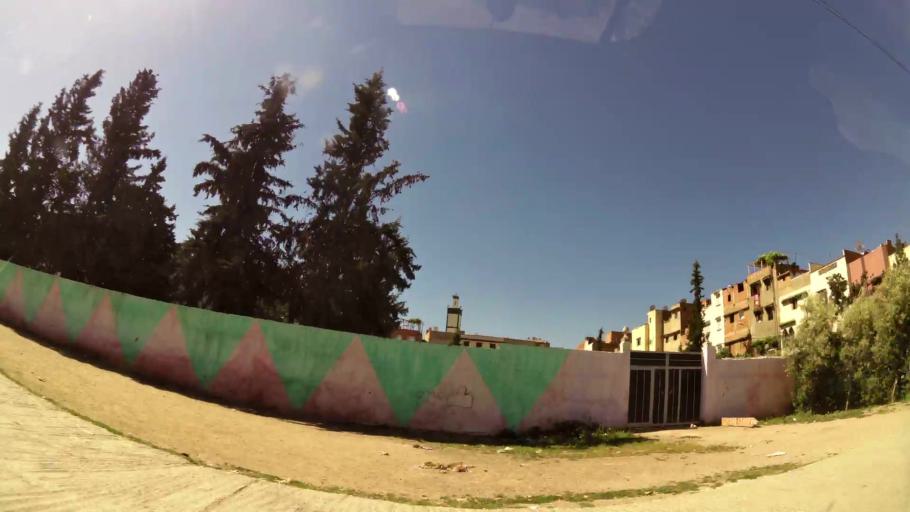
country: MA
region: Meknes-Tafilalet
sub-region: Meknes
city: Meknes
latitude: 33.9104
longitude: -5.5308
